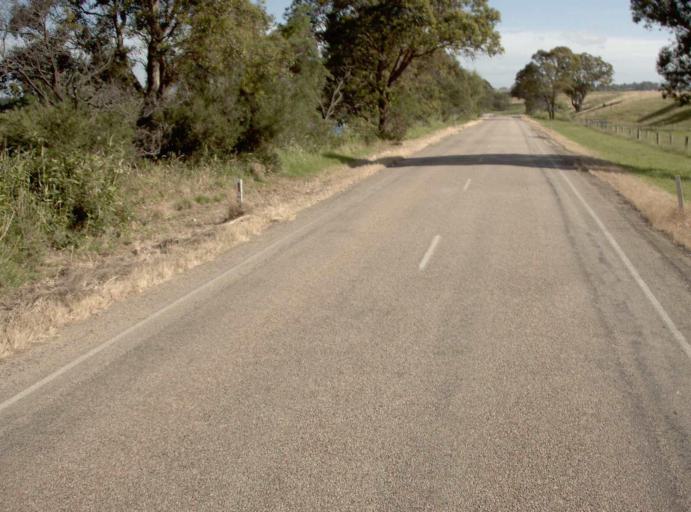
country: AU
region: Victoria
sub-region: East Gippsland
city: Lakes Entrance
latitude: -37.8366
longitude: 147.8614
